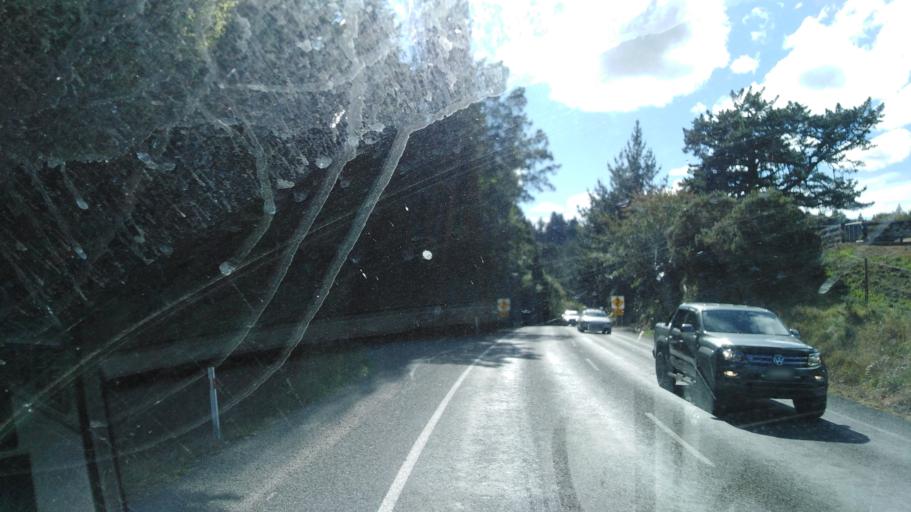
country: NZ
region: Bay of Plenty
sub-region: Tauranga City
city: Tauranga
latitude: -37.8305
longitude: 176.1232
